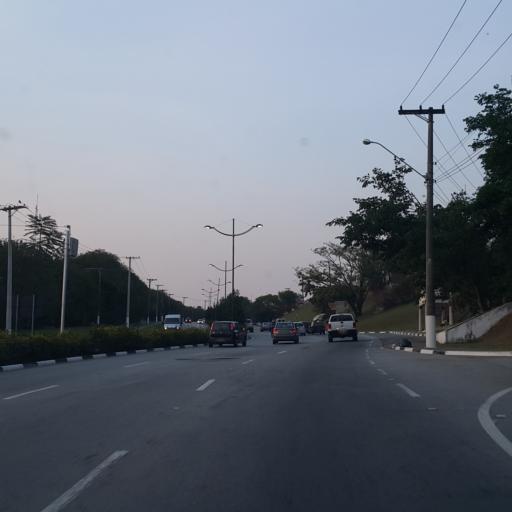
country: BR
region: Sao Paulo
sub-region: Vinhedo
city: Vinhedo
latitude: -23.0474
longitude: -46.9849
